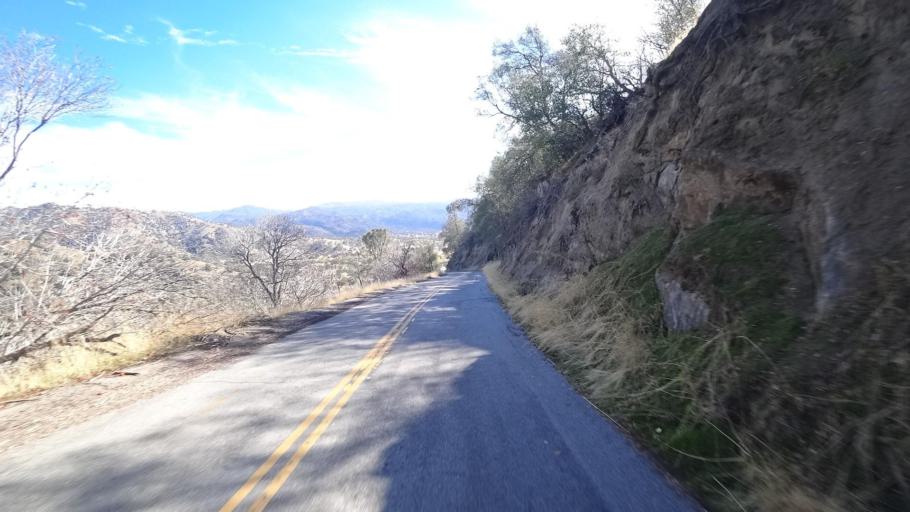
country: US
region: California
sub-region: Kern County
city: Alta Sierra
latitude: 35.6329
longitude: -118.7593
